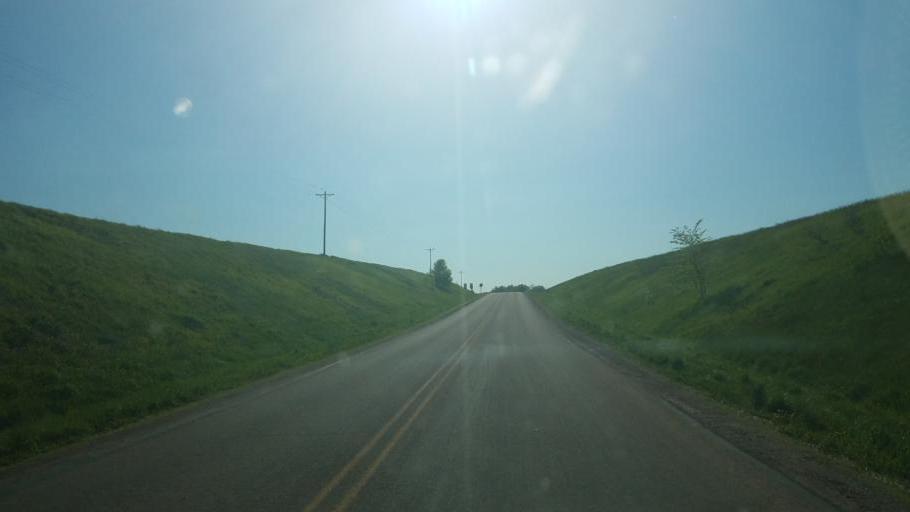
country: US
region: Wisconsin
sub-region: Vernon County
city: Hillsboro
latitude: 43.5860
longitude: -90.3527
